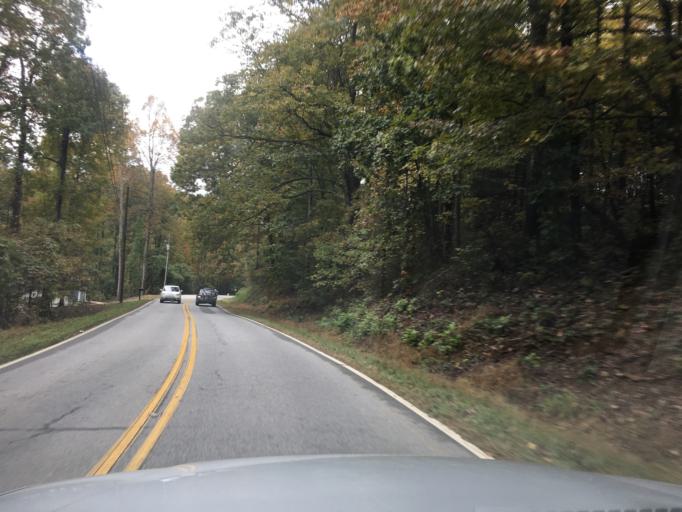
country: US
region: North Carolina
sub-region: Henderson County
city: Flat Rock
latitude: 35.2509
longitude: -82.4281
